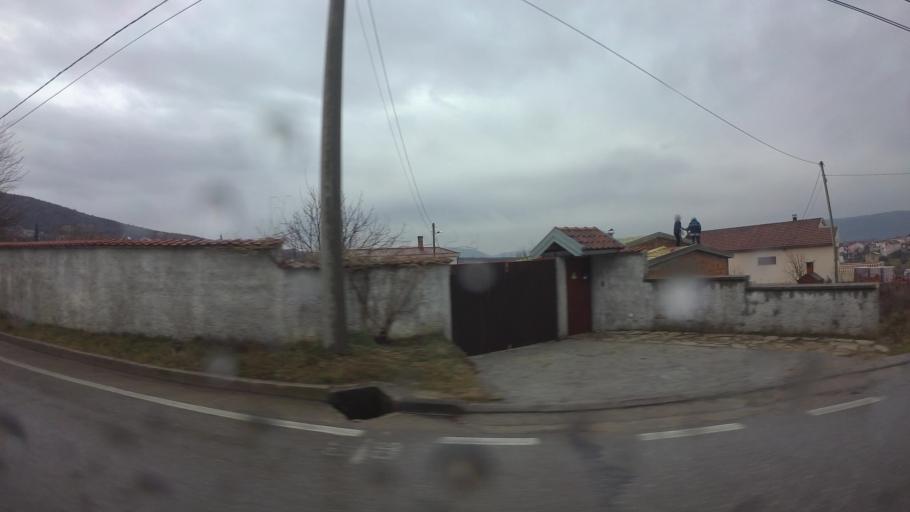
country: BA
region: Federation of Bosnia and Herzegovina
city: Blagaj
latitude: 43.2900
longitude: 17.8588
